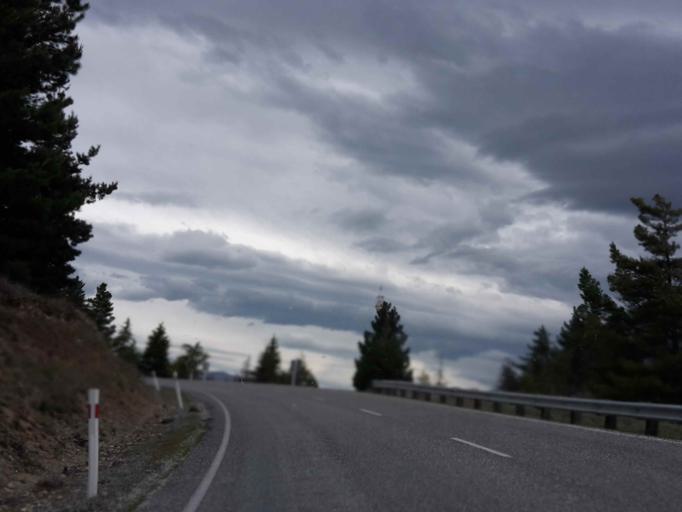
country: NZ
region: Otago
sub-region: Queenstown-Lakes District
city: Wanaka
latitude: -44.7326
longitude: 169.2867
